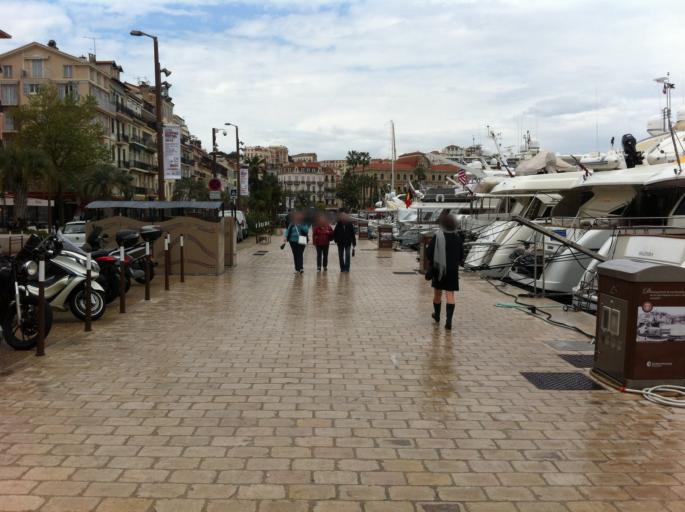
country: FR
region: Provence-Alpes-Cote d'Azur
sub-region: Departement des Alpes-Maritimes
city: Cannes
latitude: 43.5490
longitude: 7.0126
